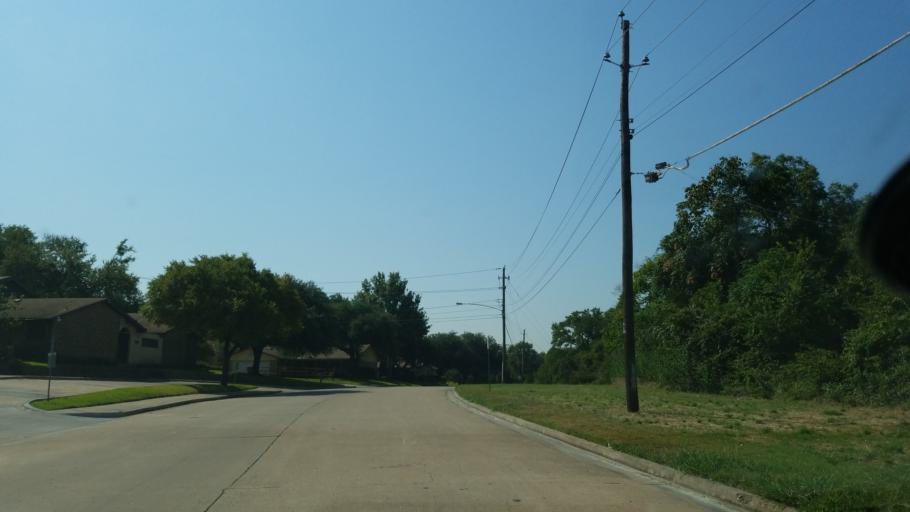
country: US
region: Texas
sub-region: Dallas County
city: Garland
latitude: 32.8779
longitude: -96.6981
